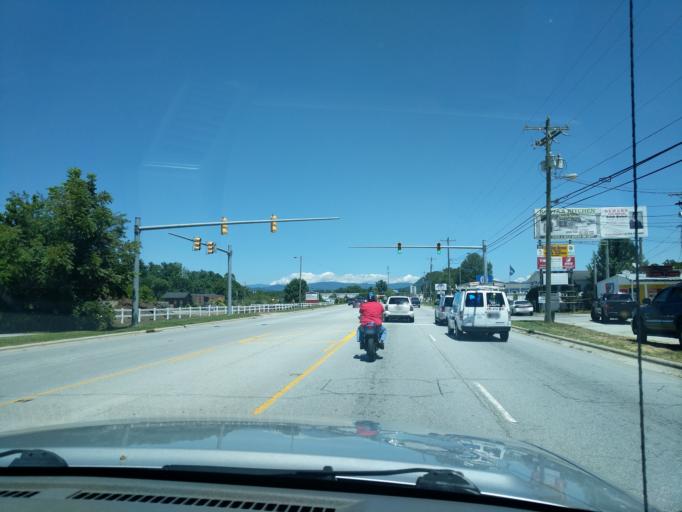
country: US
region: North Carolina
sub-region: Henderson County
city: Fletcher
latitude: 35.4106
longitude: -82.5125
